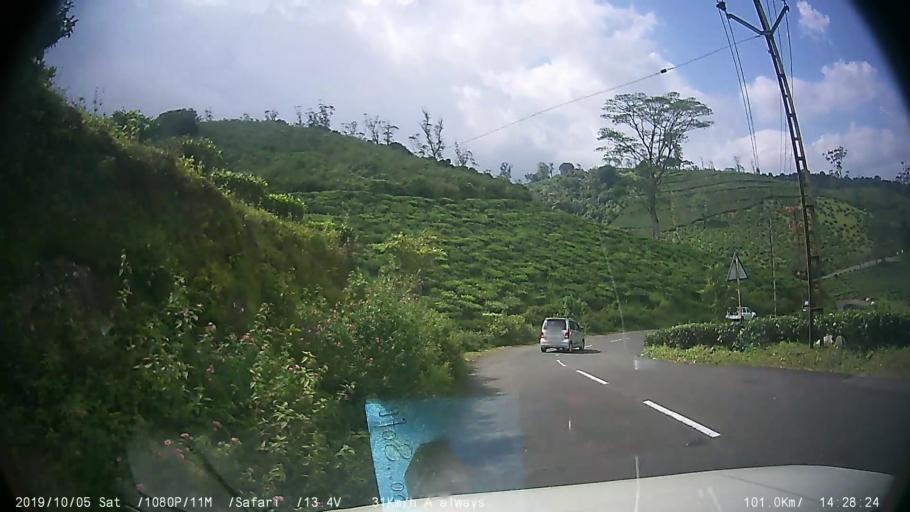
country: IN
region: Kerala
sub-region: Kottayam
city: Erattupetta
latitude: 9.6067
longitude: 76.9665
